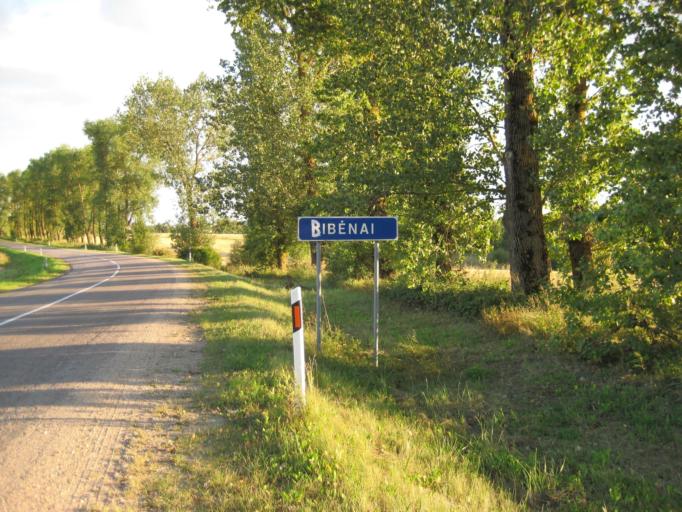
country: LT
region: Kauno apskritis
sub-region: Kaunas
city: Sargenai
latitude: 55.0681
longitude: 23.9320
